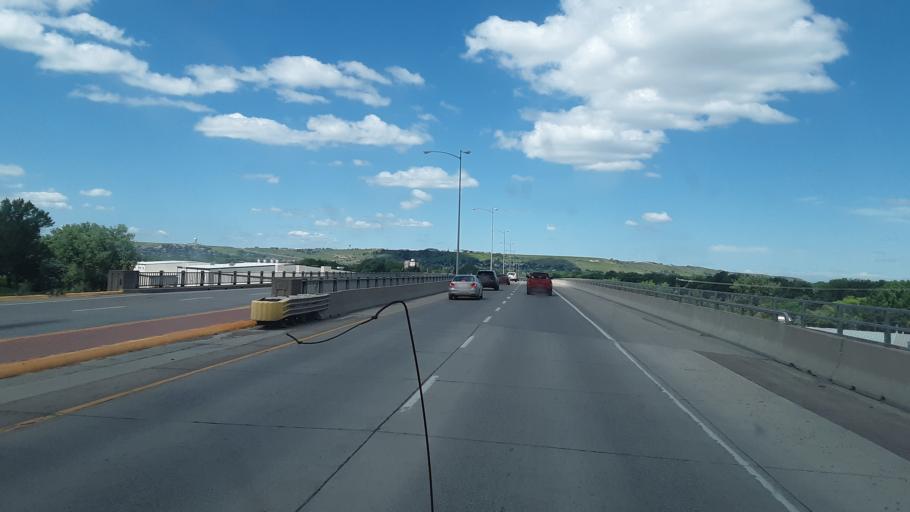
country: US
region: Montana
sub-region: Cascade County
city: Great Falls
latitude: 47.4939
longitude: -111.3060
